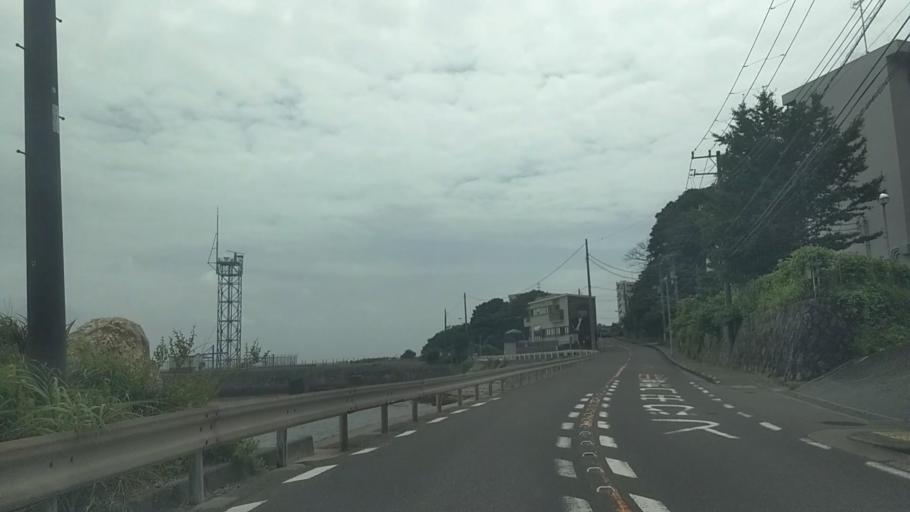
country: JP
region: Kanagawa
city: Yokosuka
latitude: 35.2458
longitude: 139.7341
